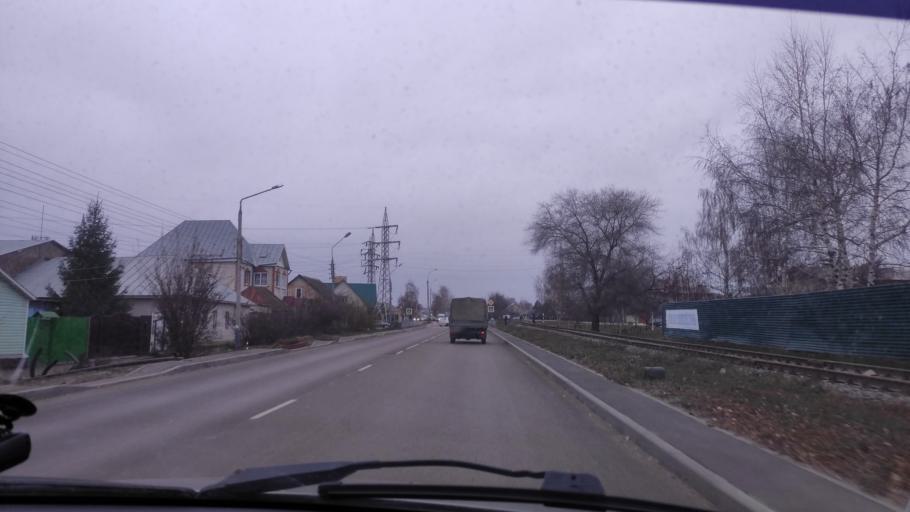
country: RU
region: Tambov
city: Tambov
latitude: 52.7211
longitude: 41.4092
